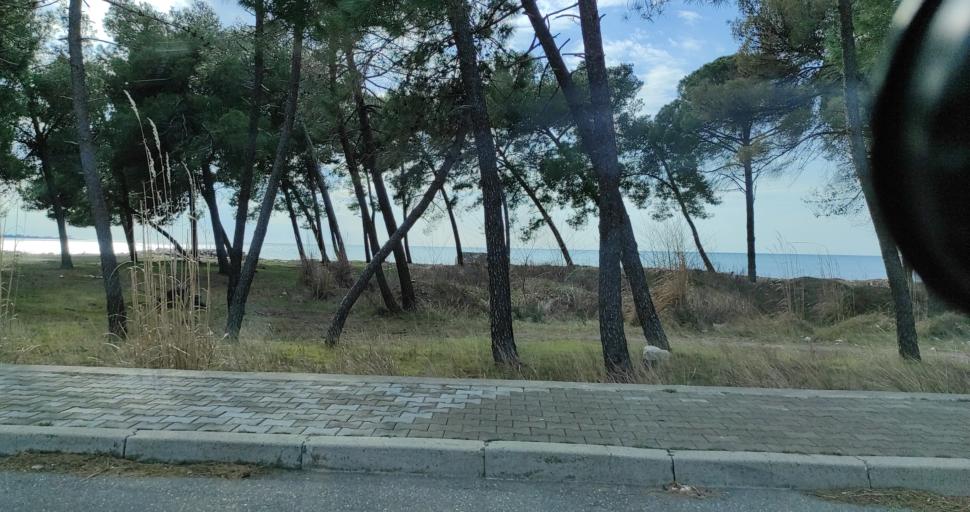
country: AL
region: Lezhe
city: Shengjin
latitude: 41.7868
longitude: 19.6035
